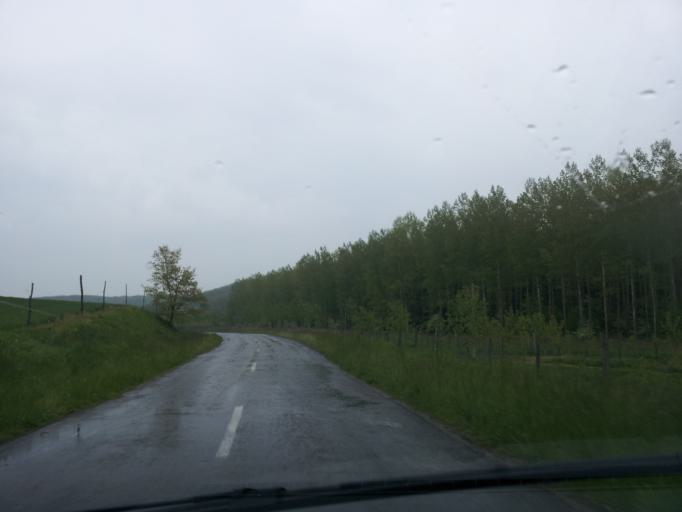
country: HU
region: Tolna
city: Szekszard
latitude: 46.2843
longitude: 18.6514
